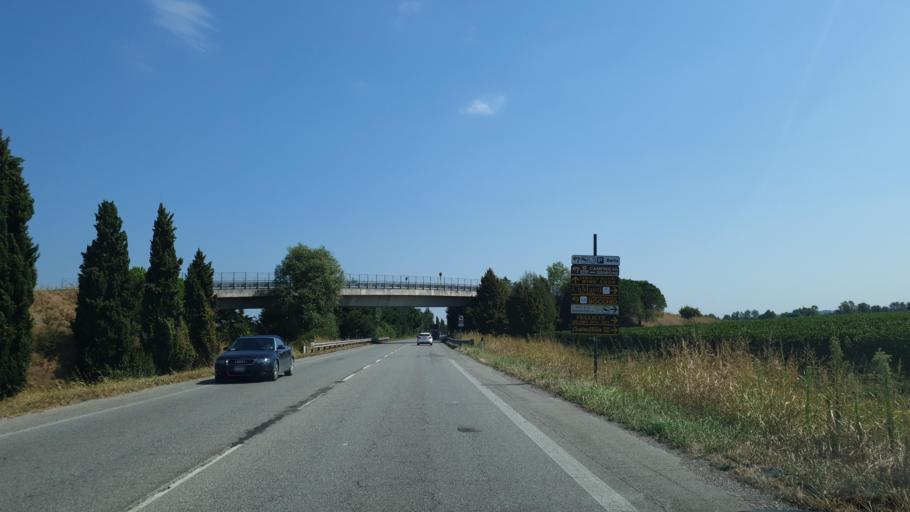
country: IT
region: Lombardy
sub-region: Provincia di Brescia
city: San Martino della Battaglia
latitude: 45.4453
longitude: 10.5811
